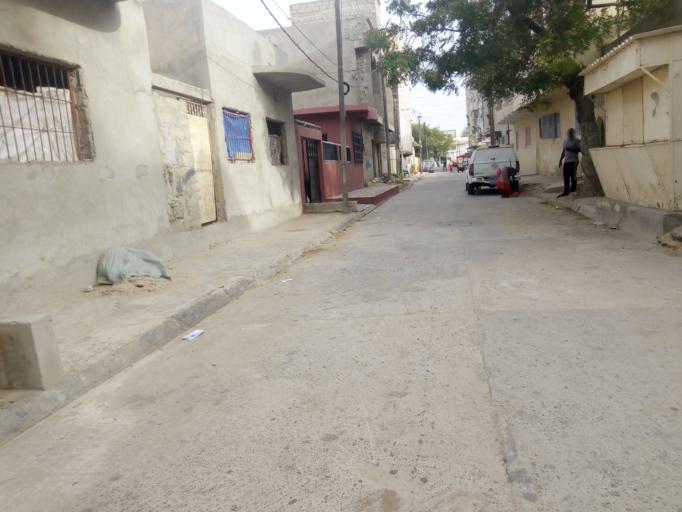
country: SN
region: Dakar
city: Dakar
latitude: 14.6988
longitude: -17.4558
